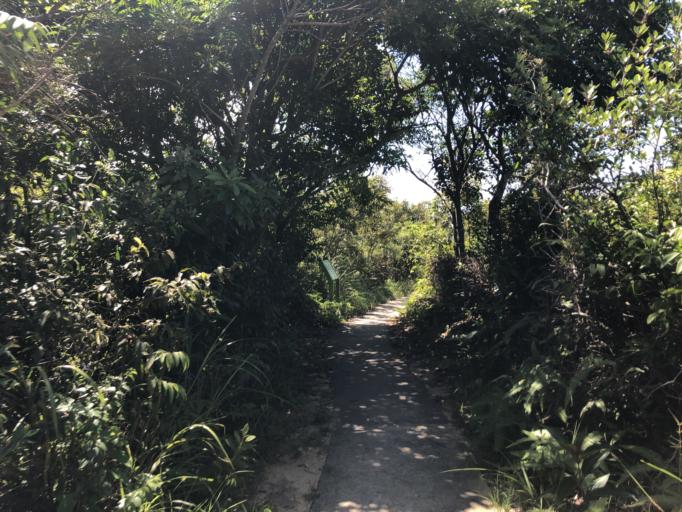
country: HK
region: Tuen Mun
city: Tuen Mun
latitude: 22.2840
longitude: 113.9831
